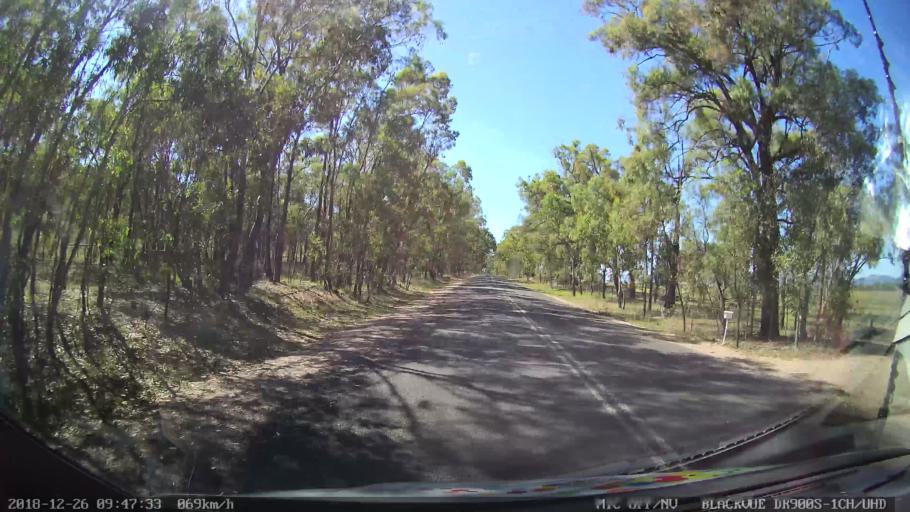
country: AU
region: New South Wales
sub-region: Mid-Western Regional
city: Kandos
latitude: -32.9802
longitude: 150.1069
